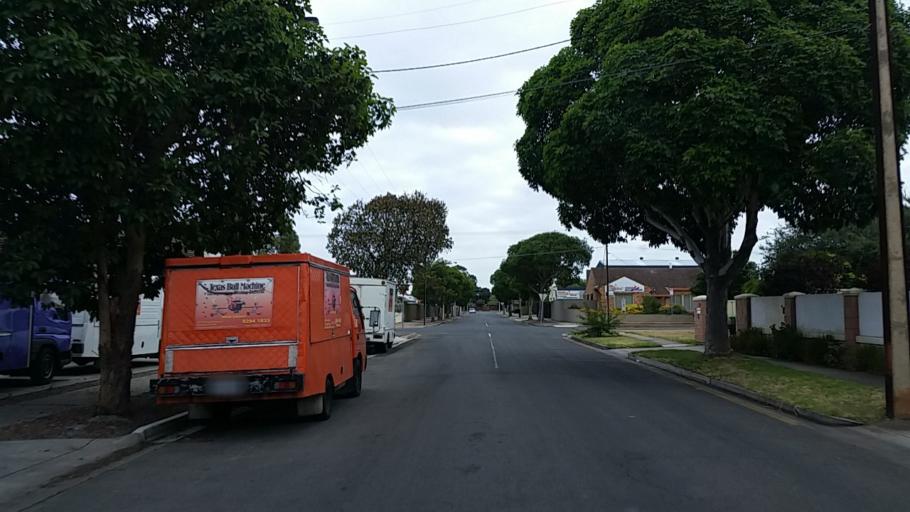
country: AU
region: South Australia
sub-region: Holdfast Bay
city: North Brighton
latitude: -34.9995
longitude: 138.5244
